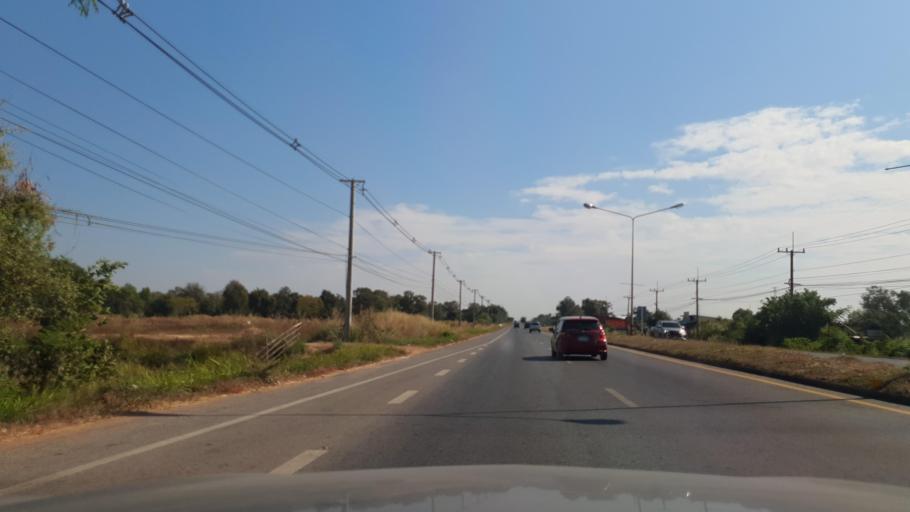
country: TH
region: Maha Sarakham
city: Chiang Yuen
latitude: 16.3730
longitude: 103.1464
